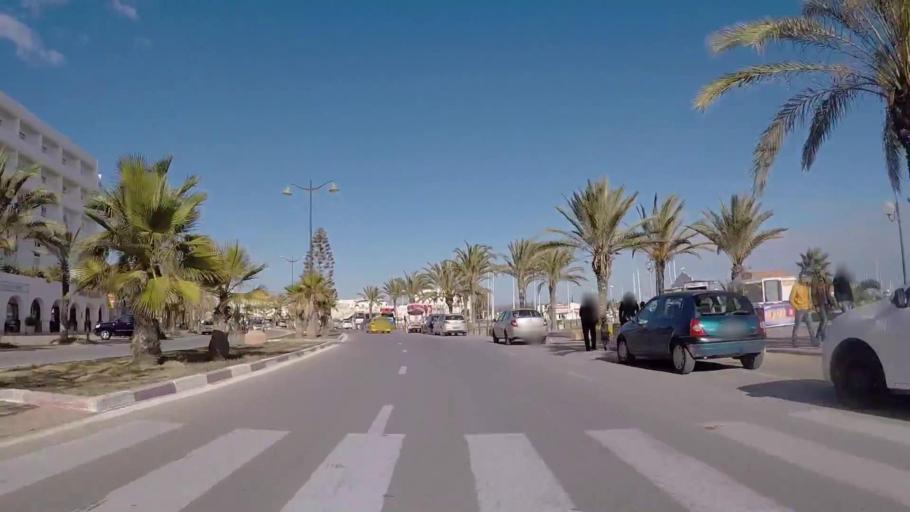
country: TN
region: Nabul
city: Al Hammamat
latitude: 36.3695
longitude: 10.5406
